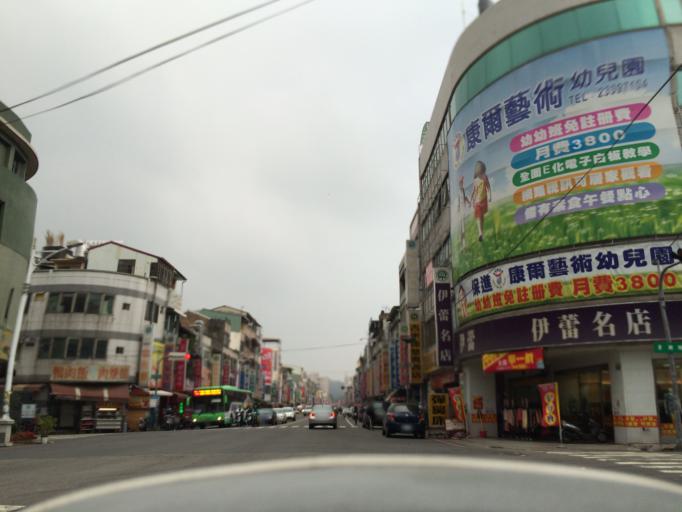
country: TW
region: Taiwan
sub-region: Taichung City
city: Taichung
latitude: 24.0681
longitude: 120.6991
